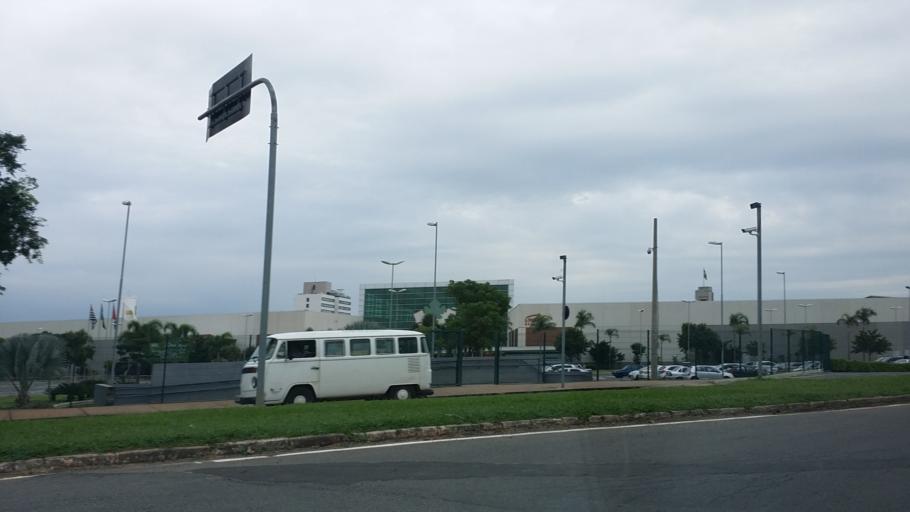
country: BR
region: Sao Paulo
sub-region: Indaiatuba
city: Indaiatuba
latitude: -23.1172
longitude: -47.2176
